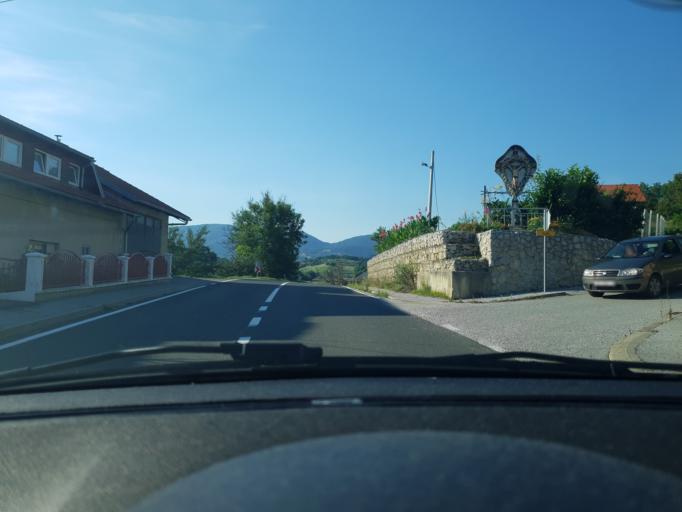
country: HR
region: Krapinsko-Zagorska
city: Mihovljan
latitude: 46.1287
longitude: 15.9380
